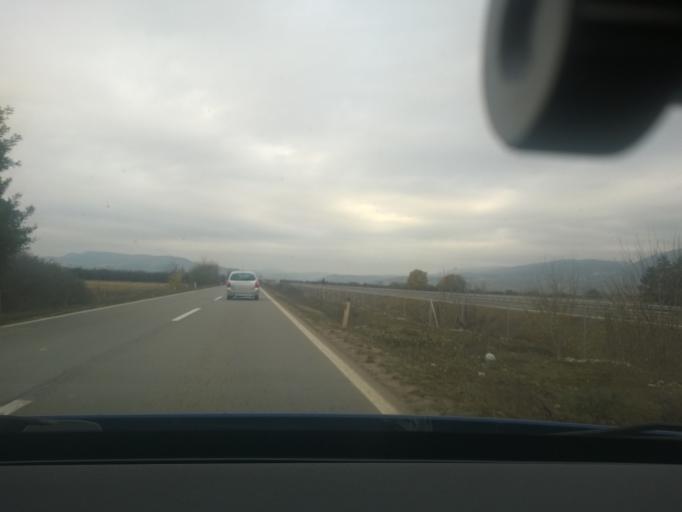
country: RS
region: Central Serbia
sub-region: Pirotski Okrug
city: Pirot
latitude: 43.0971
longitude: 22.6457
